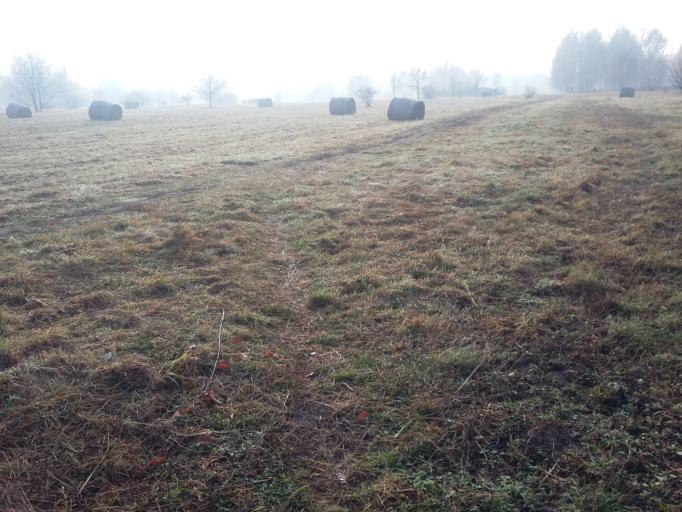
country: PL
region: Lodz Voivodeship
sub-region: Powiat pabianicki
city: Ksawerow
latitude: 51.7338
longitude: 19.3885
